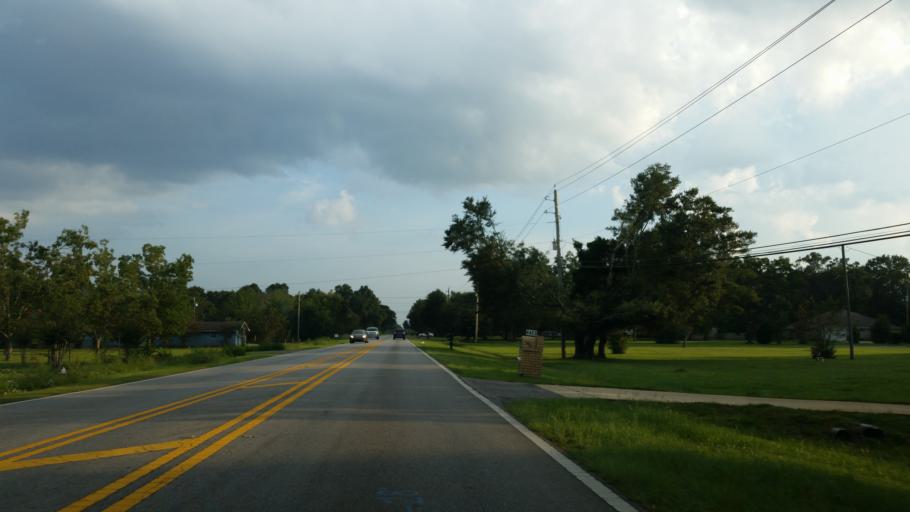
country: US
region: Florida
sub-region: Santa Rosa County
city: Pace
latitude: 30.5987
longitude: -87.1114
